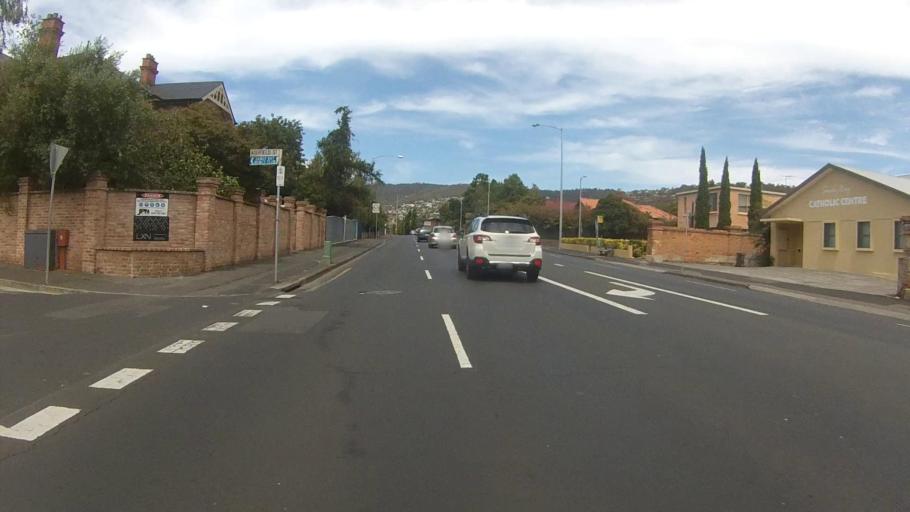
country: AU
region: Tasmania
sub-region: Hobart
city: Sandy Bay
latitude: -42.8968
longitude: 147.3287
